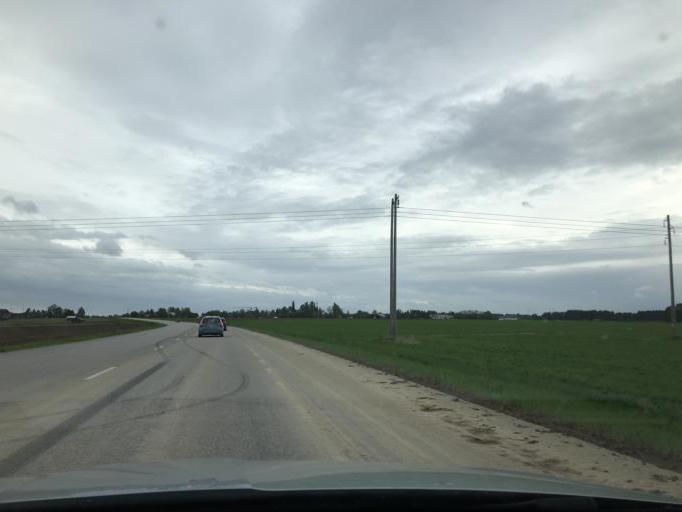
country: SE
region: Norrbotten
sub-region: Pitea Kommun
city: Bergsviken
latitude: 65.3627
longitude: 21.4059
